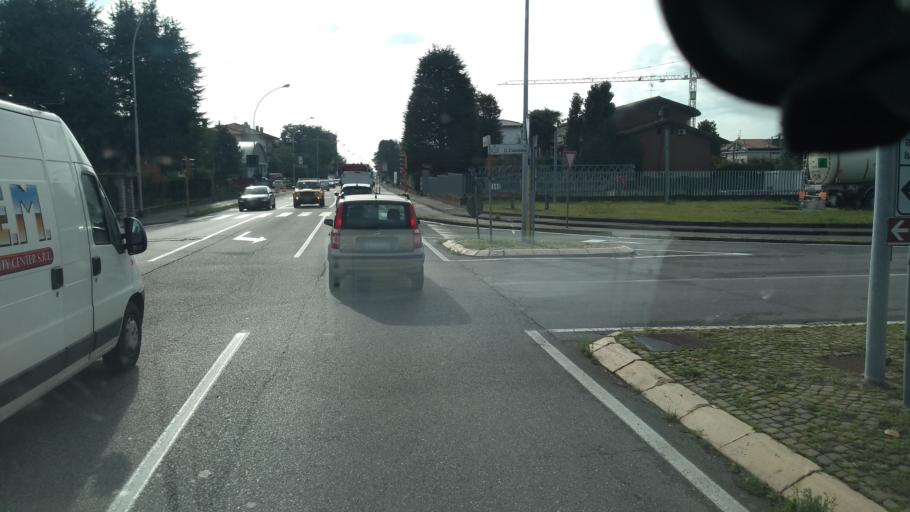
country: IT
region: Lombardy
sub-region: Provincia di Bergamo
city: Urgnano
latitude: 45.6021
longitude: 9.6983
